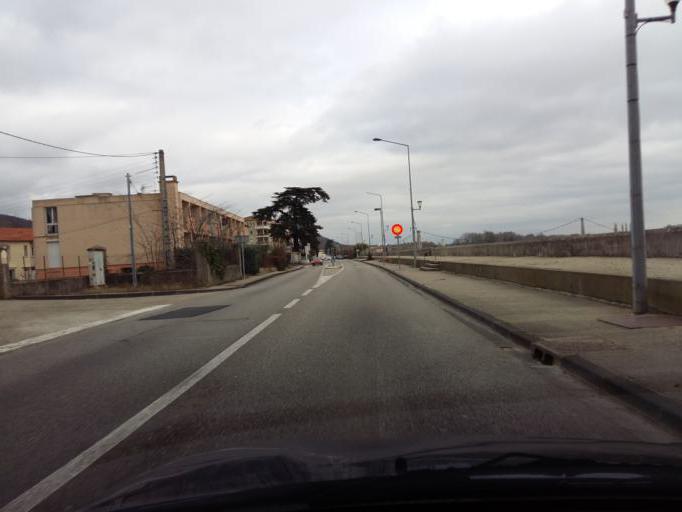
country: FR
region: Rhone-Alpes
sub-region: Departement de l'Ardeche
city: La Voulte-sur-Rhone
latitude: 44.7956
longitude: 4.7787
